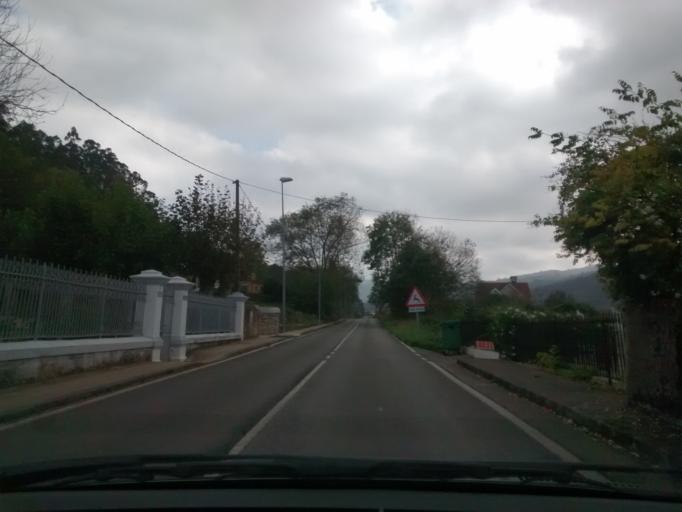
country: ES
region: Cantabria
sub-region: Provincia de Cantabria
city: Entrambasaguas
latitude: 43.3505
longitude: -3.6990
